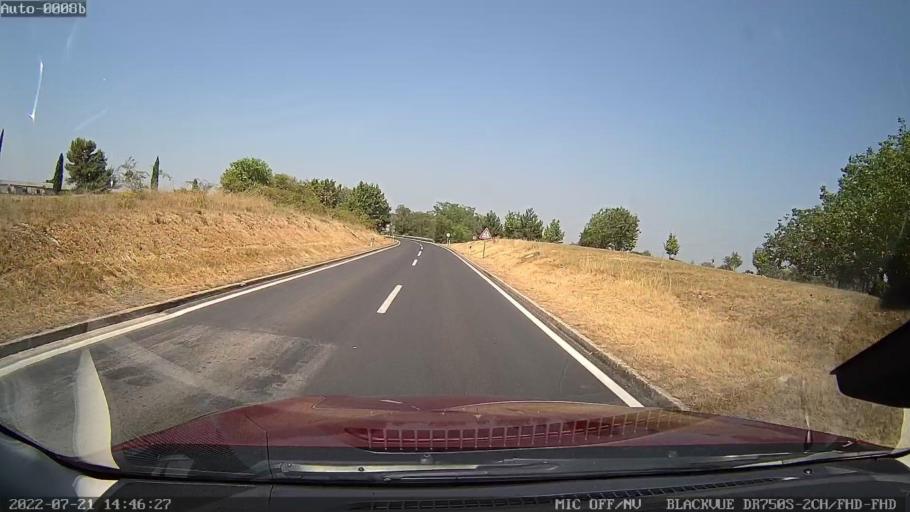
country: HR
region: Istarska
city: Pazin
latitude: 45.1369
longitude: 13.8999
